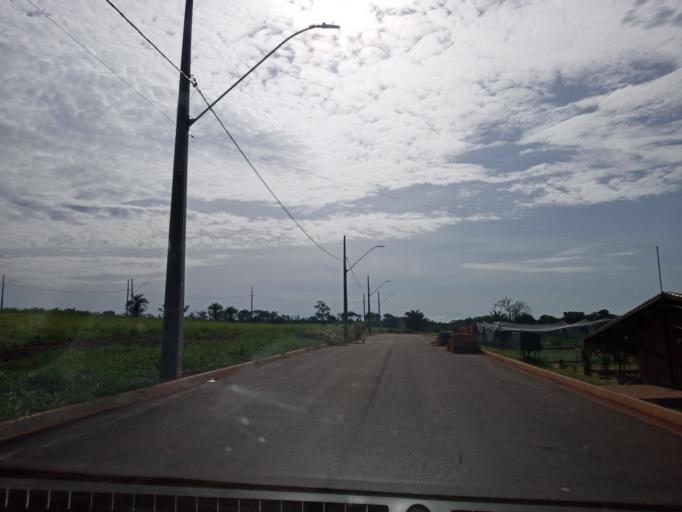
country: BR
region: Goias
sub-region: Itumbiara
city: Itumbiara
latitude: -18.4330
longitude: -49.1816
